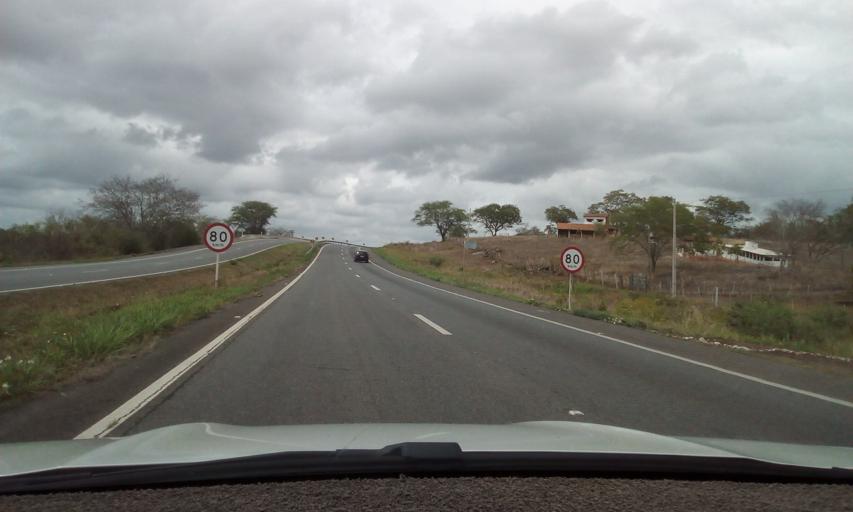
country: BR
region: Paraiba
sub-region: Fagundes
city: Fagundes
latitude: -7.2765
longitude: -35.7298
